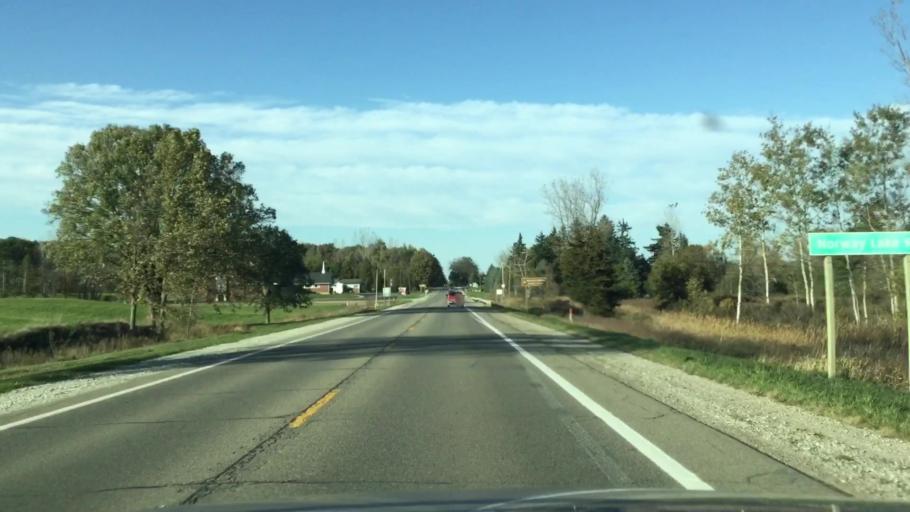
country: US
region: Michigan
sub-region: Lapeer County
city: Barnes Lake-Millers Lake
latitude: 43.1443
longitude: -83.3110
